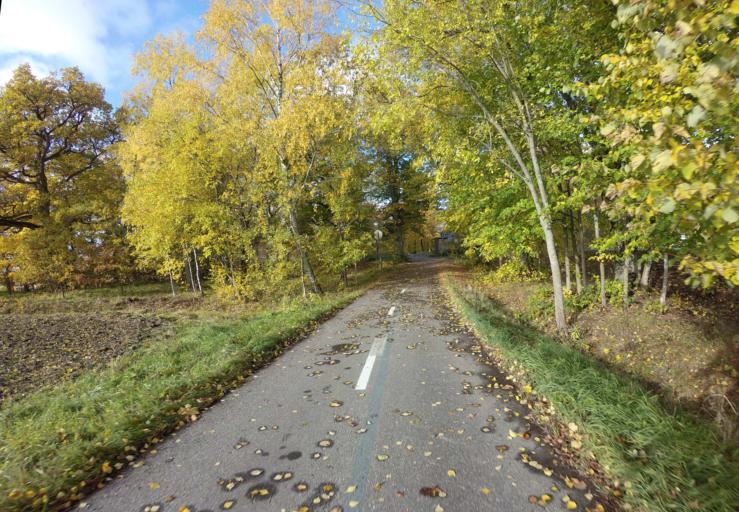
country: FI
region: Varsinais-Suomi
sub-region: Turku
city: Raisio
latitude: 60.4268
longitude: 22.1423
